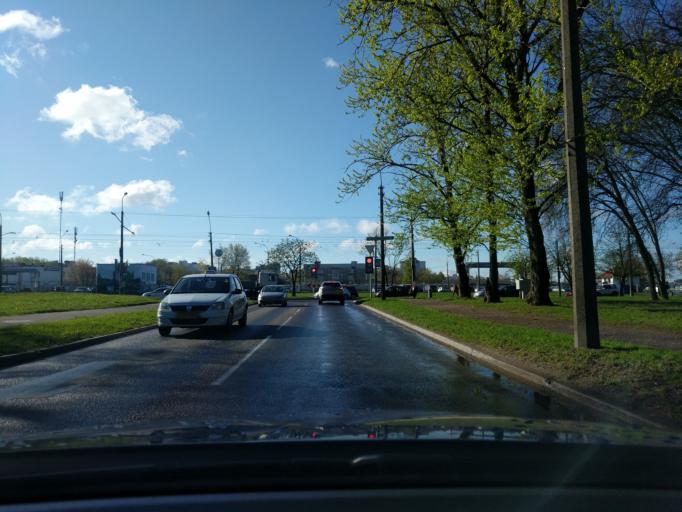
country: BY
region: Minsk
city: Novoye Medvezhino
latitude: 53.8988
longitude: 27.5071
